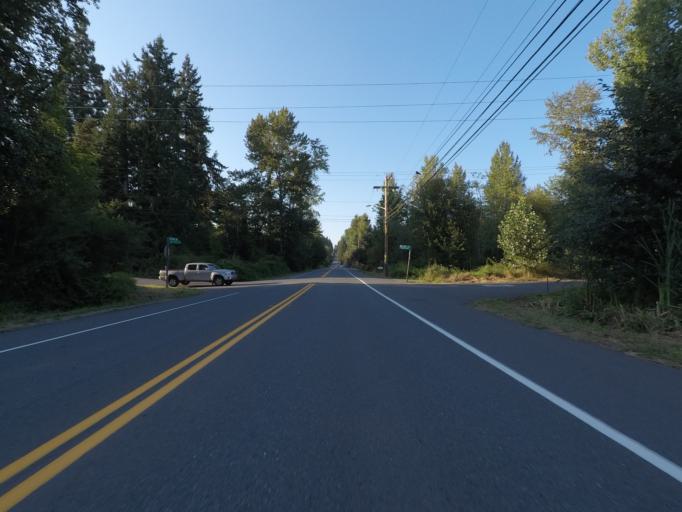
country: US
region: Washington
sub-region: King County
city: Kenmore
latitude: 47.7693
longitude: -122.2333
